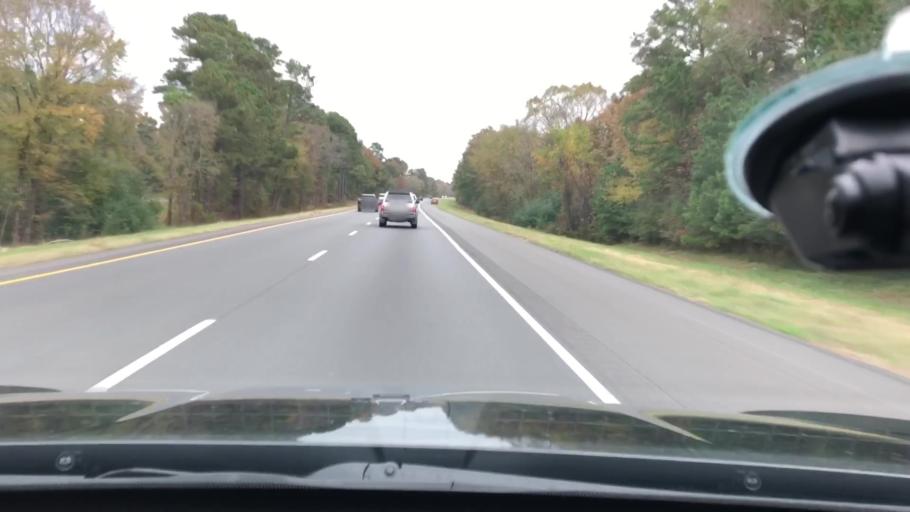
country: US
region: Arkansas
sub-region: Hempstead County
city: Hope
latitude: 33.7133
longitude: -93.5674
